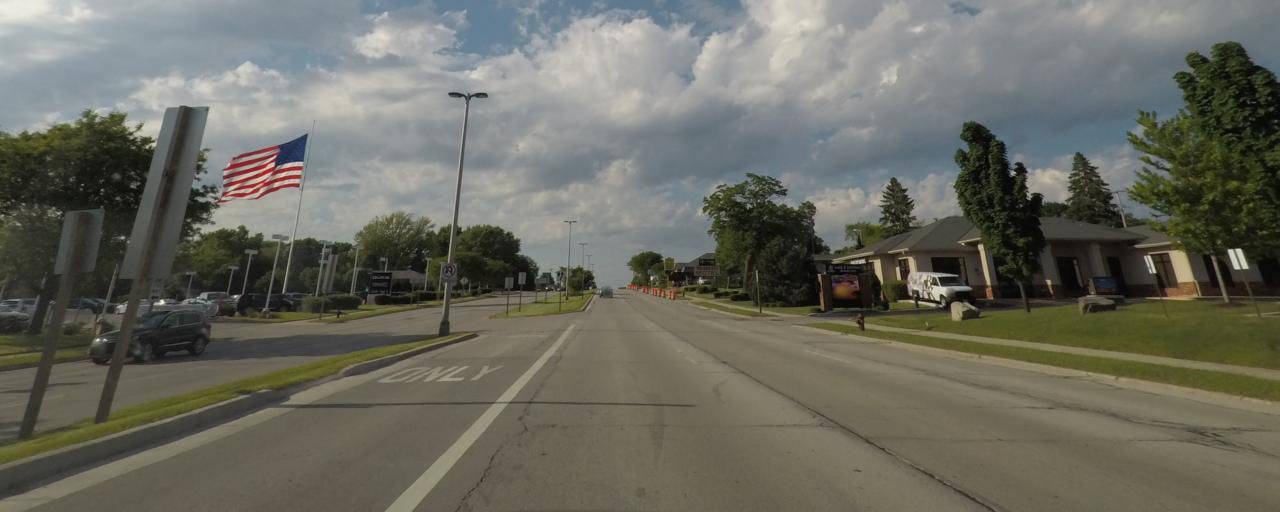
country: US
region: Wisconsin
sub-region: Milwaukee County
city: Greenfield
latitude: 42.9773
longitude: -88.0474
